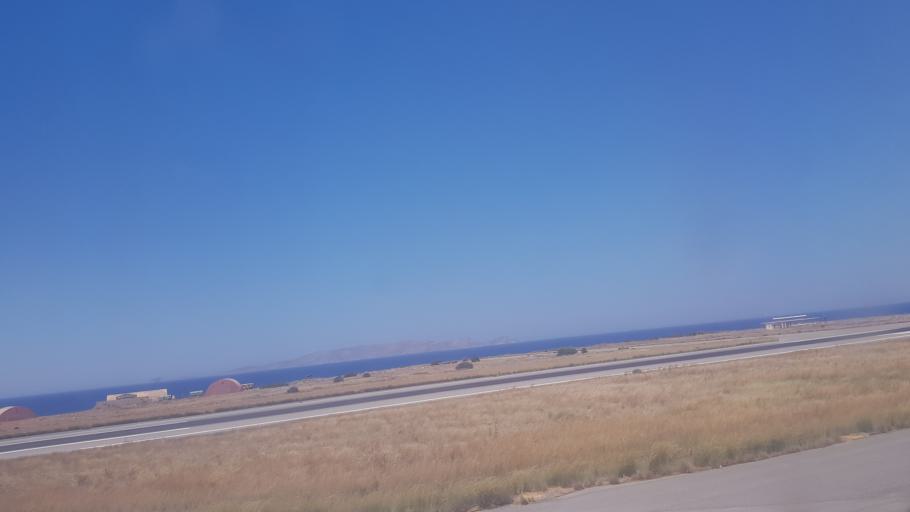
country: GR
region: Crete
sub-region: Nomos Irakleiou
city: Nea Alikarnassos
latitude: 35.3386
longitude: 25.1821
